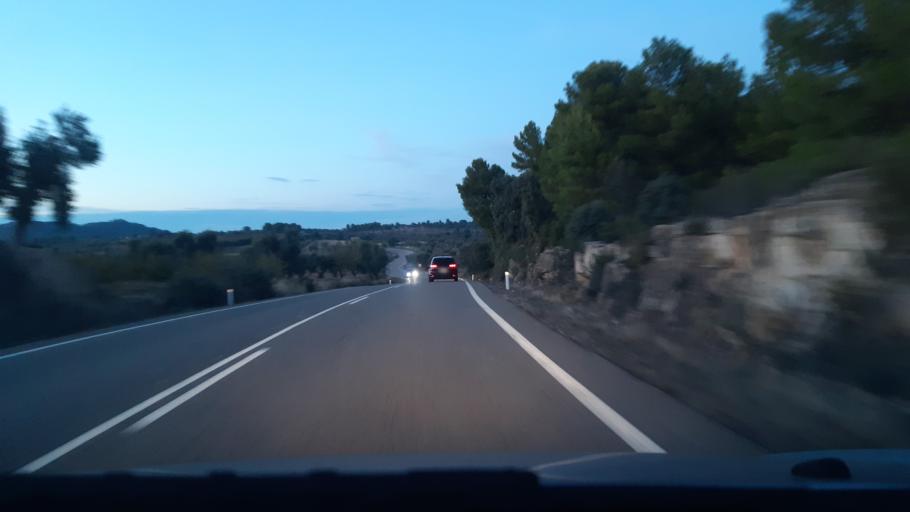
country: ES
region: Aragon
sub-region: Provincia de Teruel
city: Calaceite
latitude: 40.9865
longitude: 0.1993
